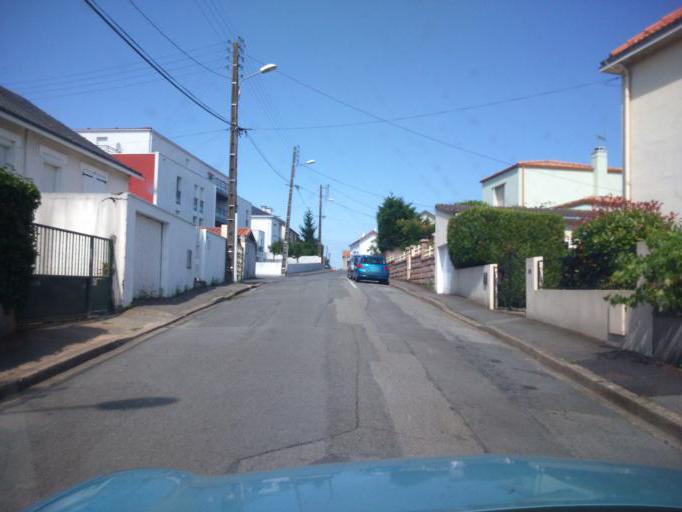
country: FR
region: Pays de la Loire
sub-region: Departement de la Loire-Atlantique
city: Saint-Sebastien-sur-Loire
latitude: 47.1959
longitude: -1.5209
